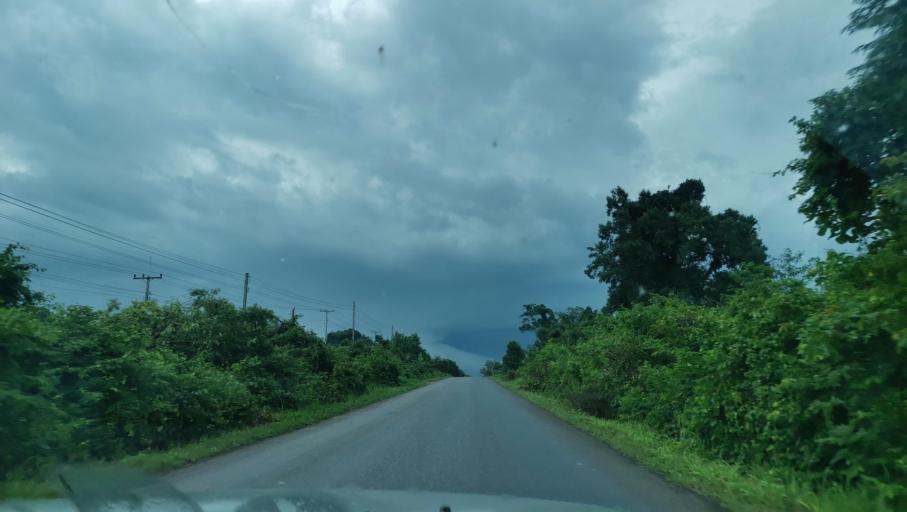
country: TH
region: Nakhon Phanom
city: Ban Phaeng
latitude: 17.8825
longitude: 104.4066
